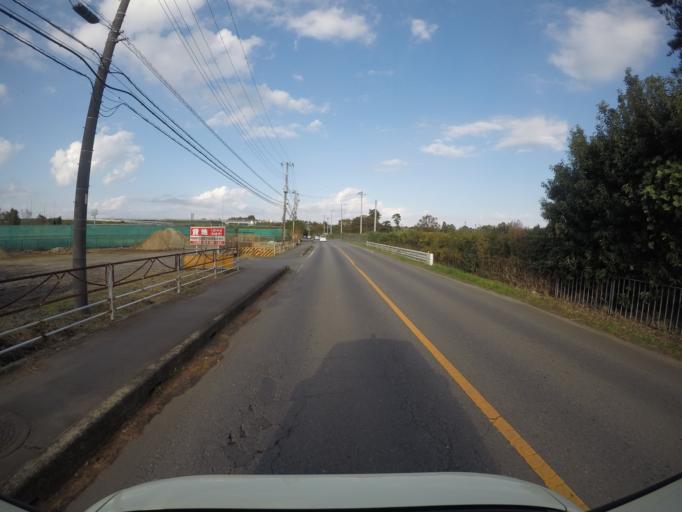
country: JP
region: Ibaraki
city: Naka
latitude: 36.0556
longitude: 140.0870
